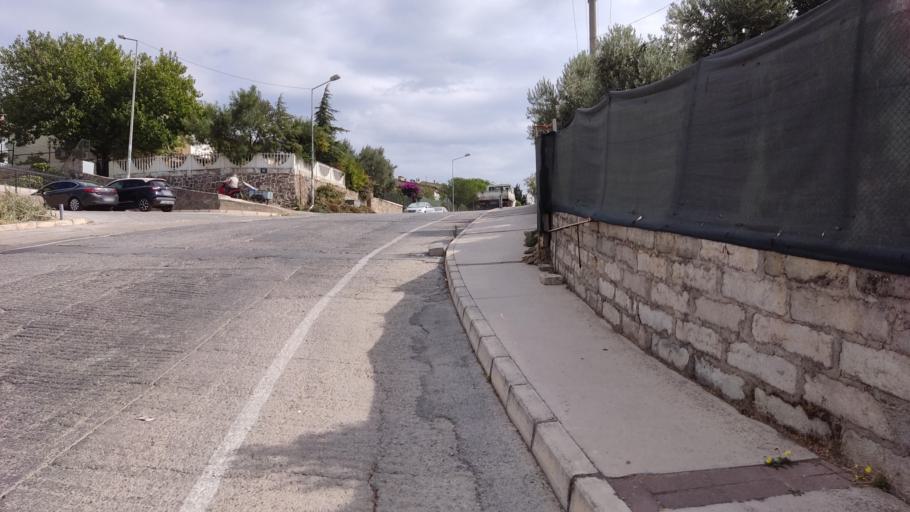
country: TR
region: Izmir
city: Karsiyaka
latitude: 38.5010
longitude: 27.0850
